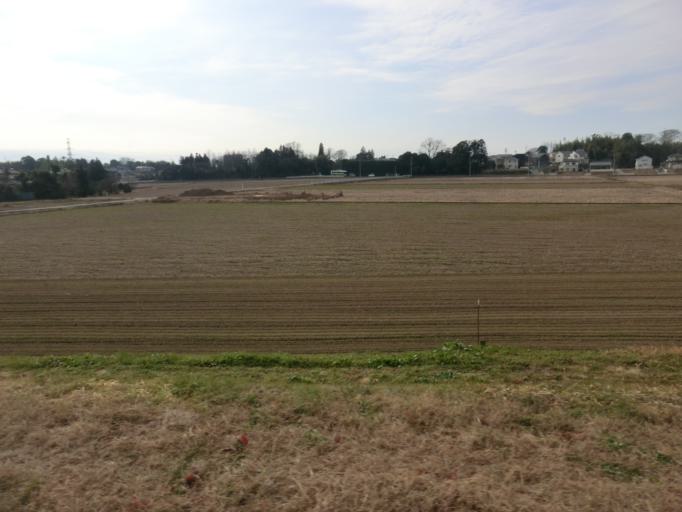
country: JP
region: Ibaraki
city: Moriya
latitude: 35.9742
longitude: 139.9957
